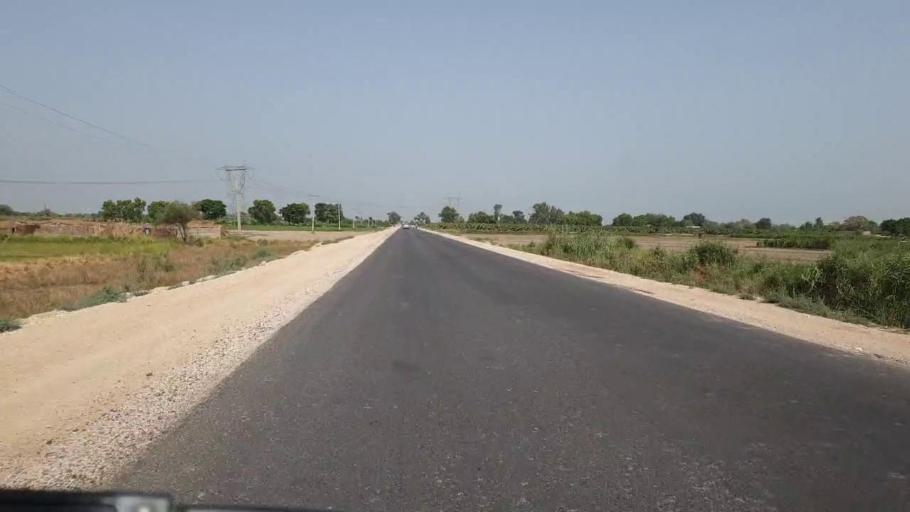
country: PK
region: Sindh
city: Sakrand
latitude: 26.2556
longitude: 68.1967
